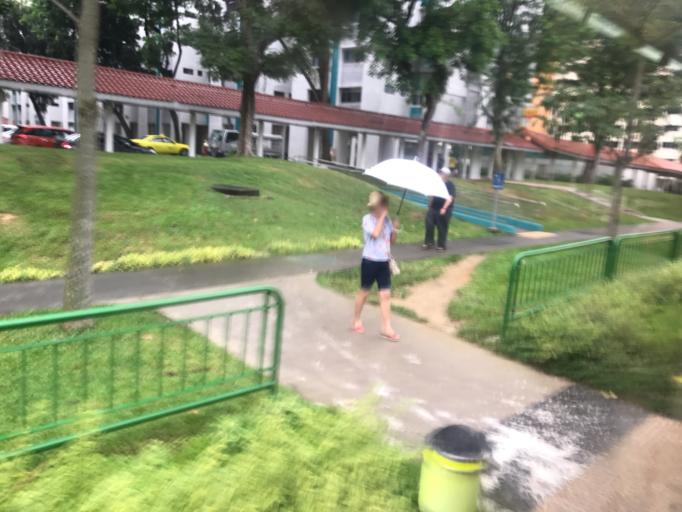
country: SG
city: Singapore
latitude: 1.3317
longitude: 103.9261
